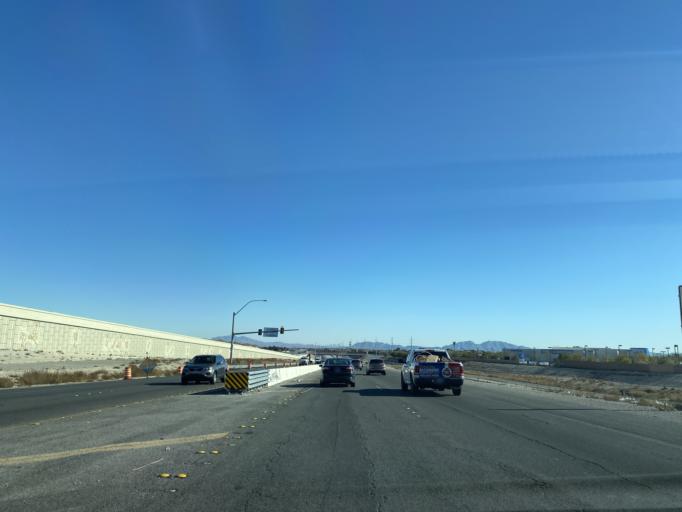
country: US
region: Nevada
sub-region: Clark County
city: Las Vegas
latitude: 36.2761
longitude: -115.2620
